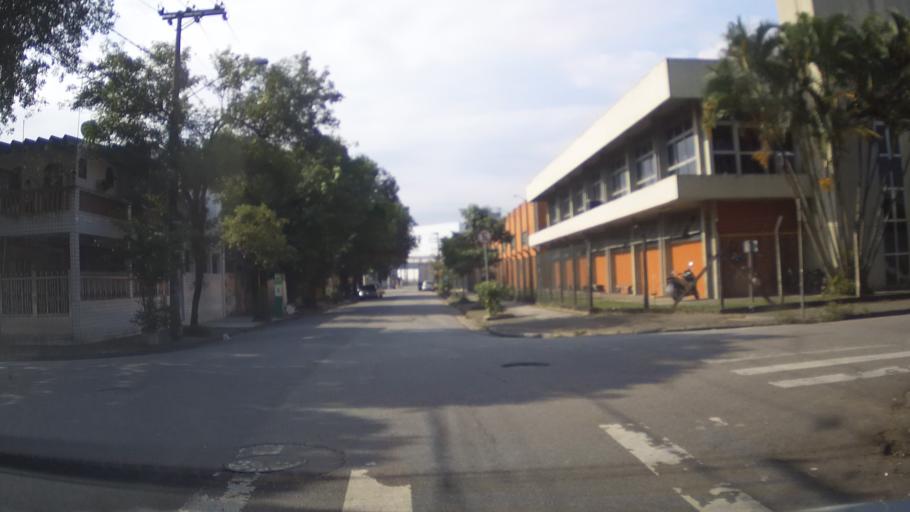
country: BR
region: Sao Paulo
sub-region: Santos
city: Santos
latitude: -23.9654
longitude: -46.3059
